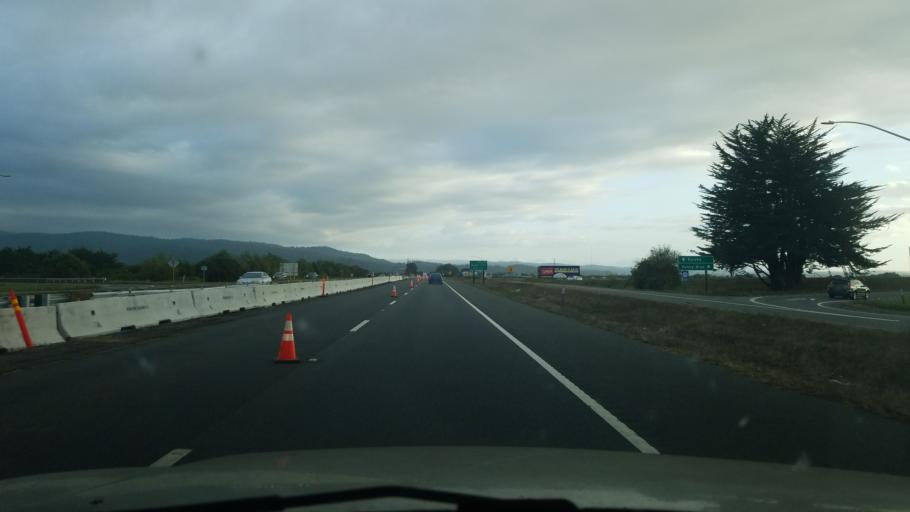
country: US
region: California
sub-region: Humboldt County
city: Arcata
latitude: 40.8627
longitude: -124.0829
